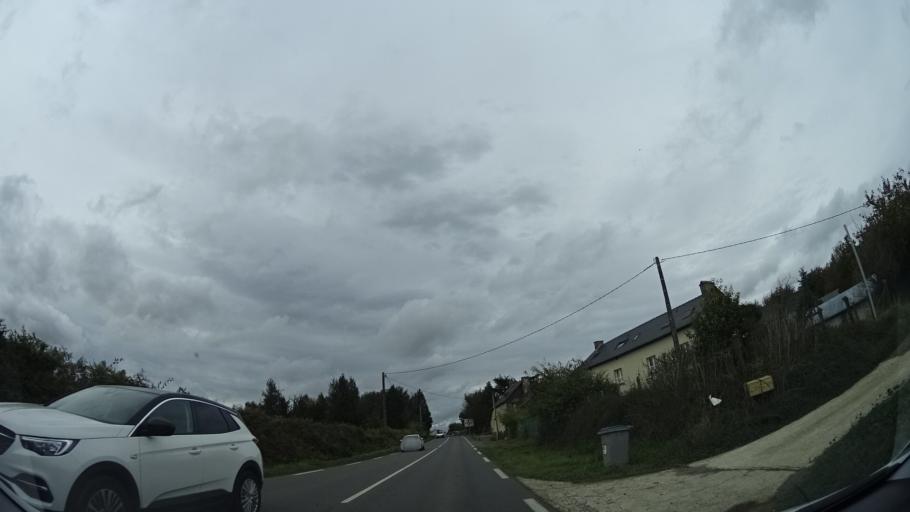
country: FR
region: Brittany
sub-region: Departement d'Ille-et-Vilaine
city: La Meziere
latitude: 48.2076
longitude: -1.7524
